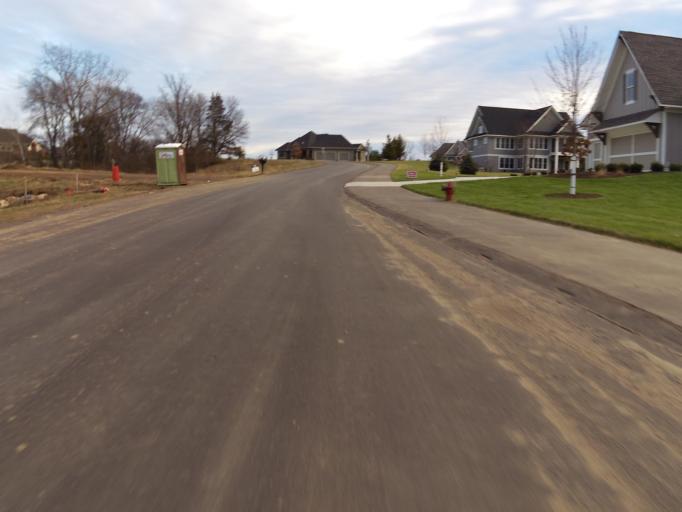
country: US
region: Minnesota
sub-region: Washington County
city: Bayport
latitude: 45.0011
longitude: -92.7986
